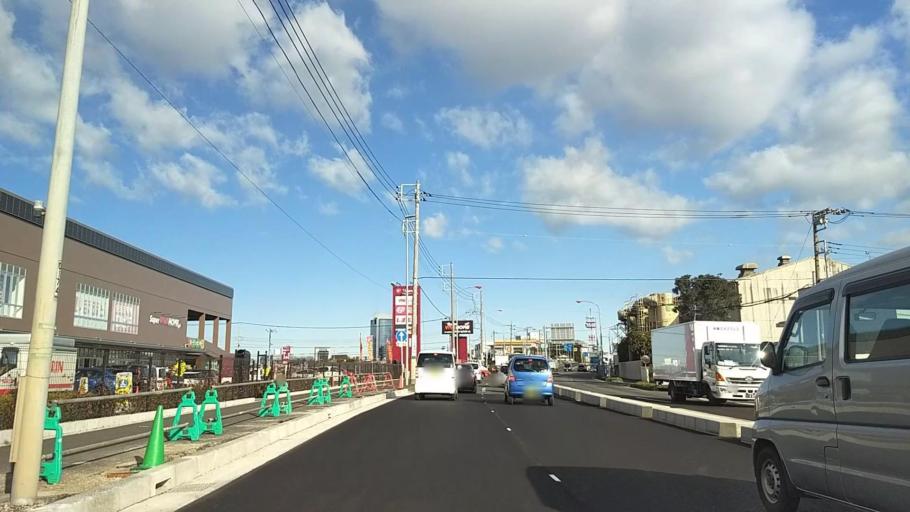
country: JP
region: Kanagawa
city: Atsugi
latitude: 35.4096
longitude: 139.3616
